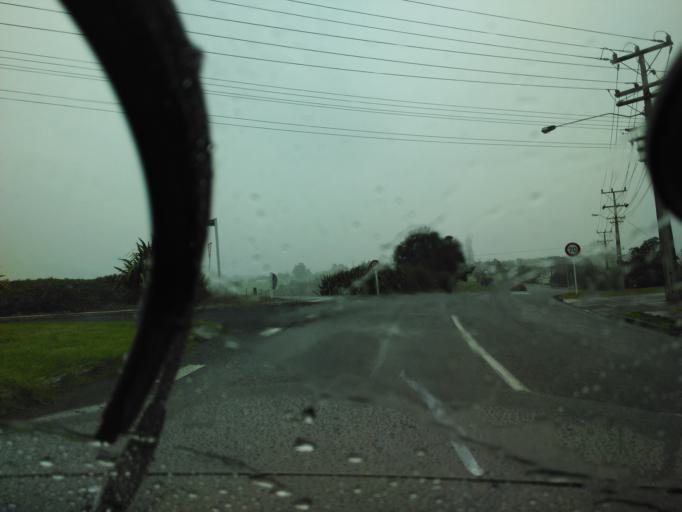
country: NZ
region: Auckland
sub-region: Auckland
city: Wellsford
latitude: -36.2988
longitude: 174.5205
